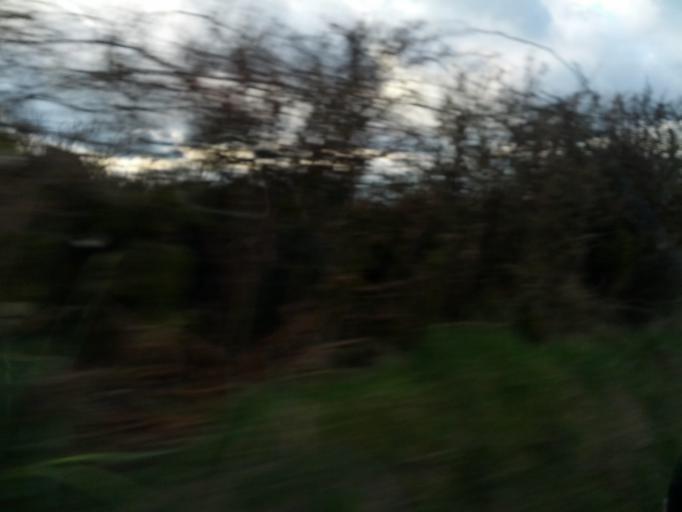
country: IE
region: Connaught
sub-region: County Galway
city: Athenry
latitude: 53.4211
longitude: -8.7540
